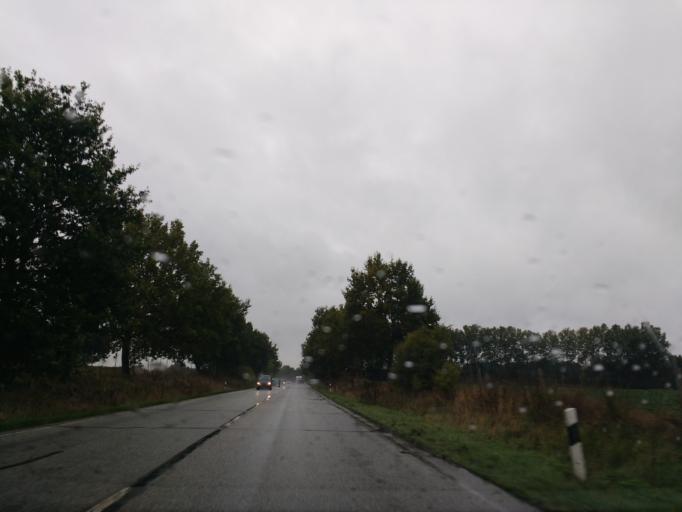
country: DE
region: Schleswig-Holstein
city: Susel
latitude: 54.0689
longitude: 10.7115
